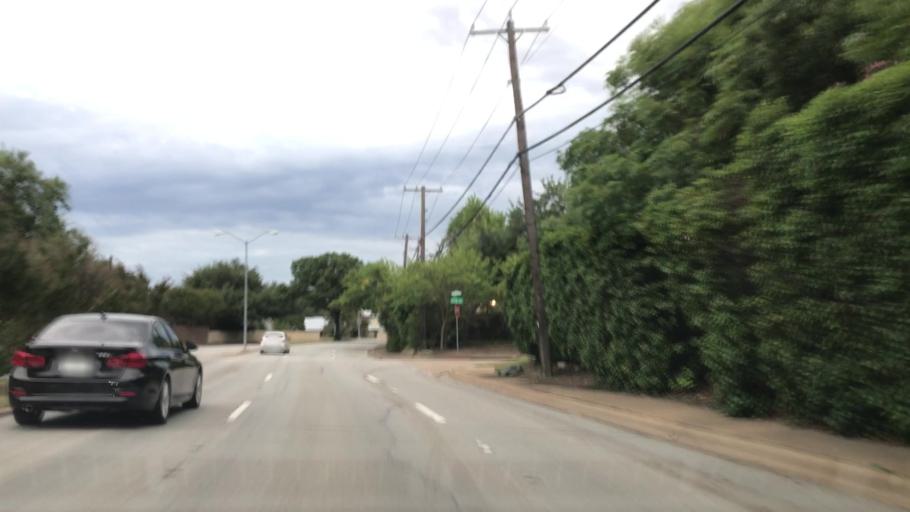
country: US
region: Texas
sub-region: Dallas County
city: University Park
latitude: 32.8941
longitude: -96.7876
